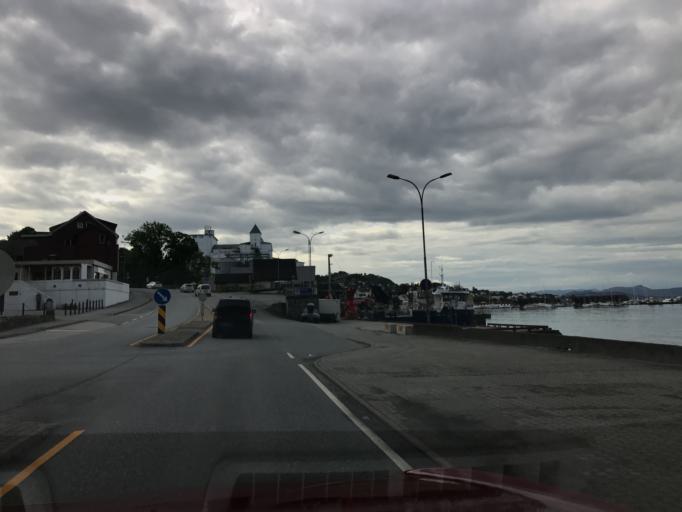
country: NO
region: Rogaland
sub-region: Strand
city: Tau
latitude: 59.0656
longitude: 5.9100
